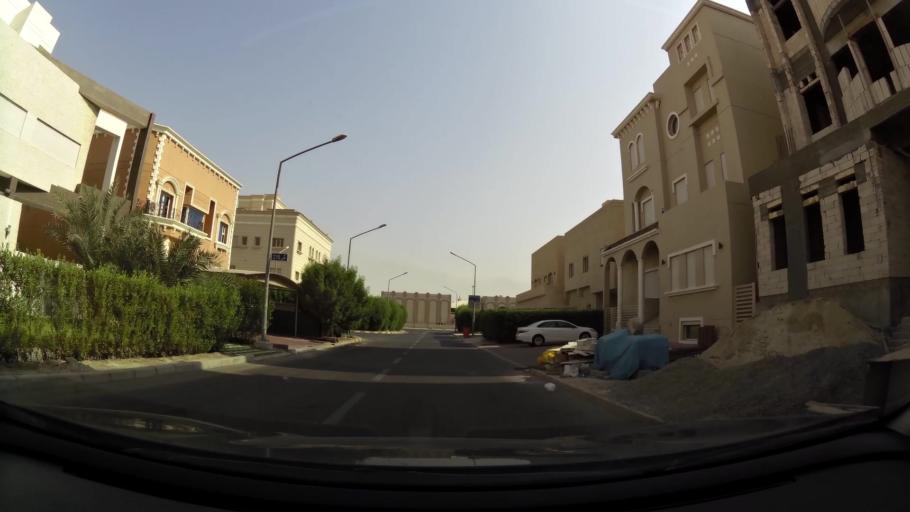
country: KW
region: Muhafazat al Jahra'
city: Al Jahra'
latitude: 29.3373
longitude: 47.7691
